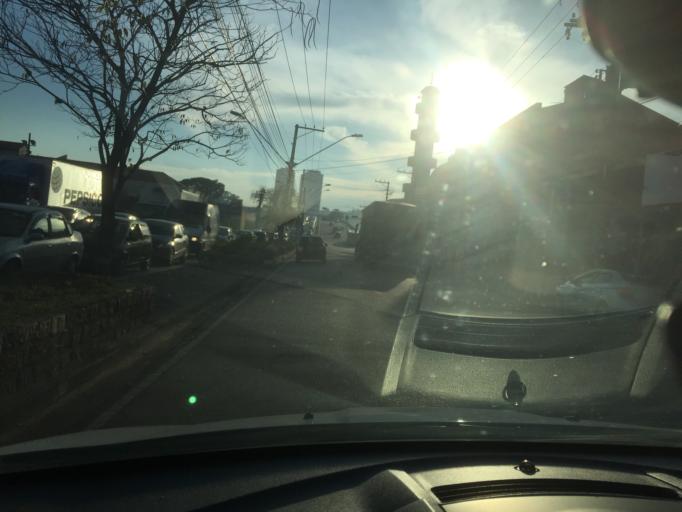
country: BR
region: Sao Paulo
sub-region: Jundiai
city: Jundiai
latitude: -23.1934
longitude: -46.8772
